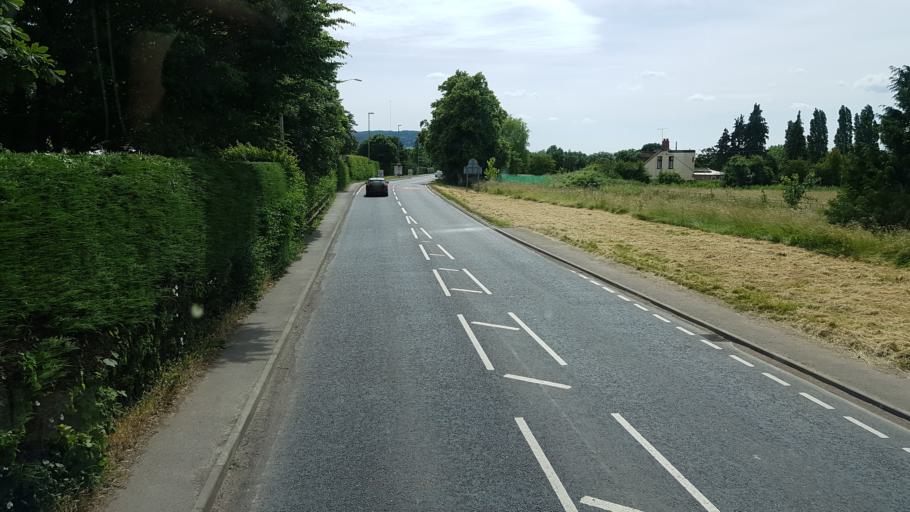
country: GB
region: England
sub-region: Gloucestershire
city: Shurdington
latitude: 51.8613
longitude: -2.1219
